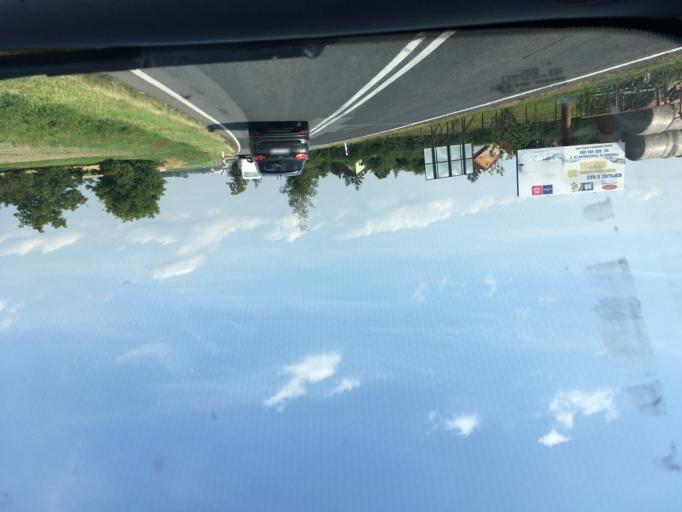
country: PL
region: Opole Voivodeship
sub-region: Powiat prudnicki
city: Prudnik
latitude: 50.3492
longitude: 17.5558
